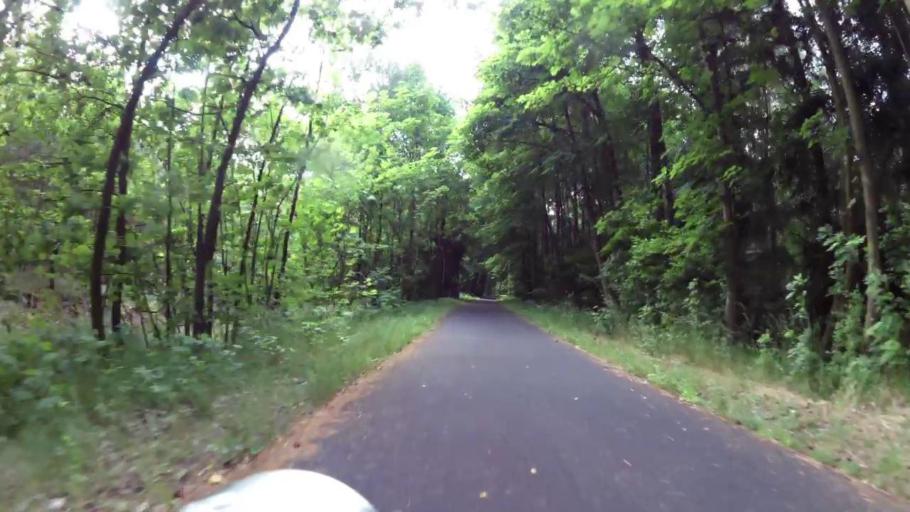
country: PL
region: Kujawsko-Pomorskie
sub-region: Powiat chelminski
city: Unislaw
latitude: 53.1875
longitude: 18.3736
